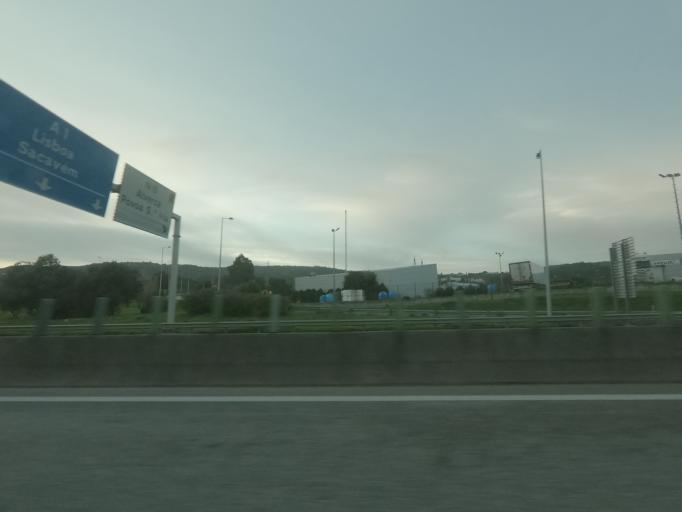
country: PT
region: Lisbon
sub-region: Vila Franca de Xira
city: Sobralinho
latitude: 38.8951
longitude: -9.0480
